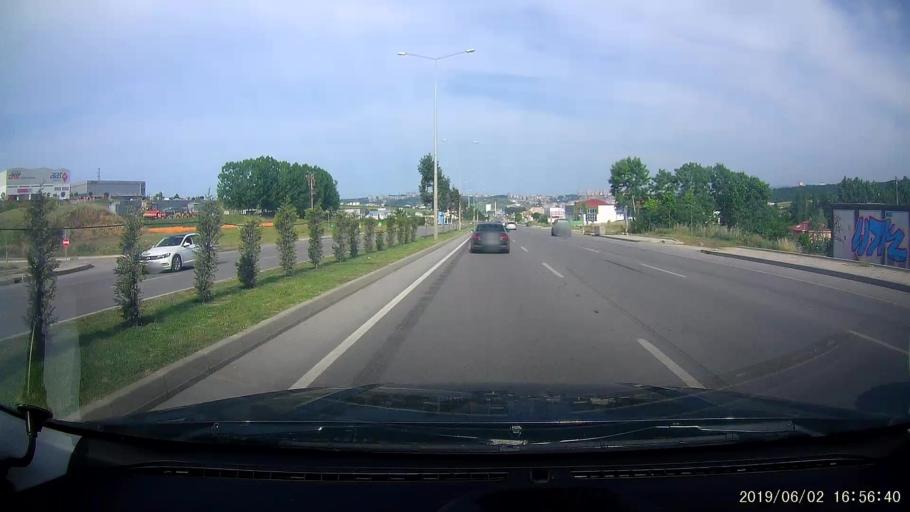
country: TR
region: Samsun
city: Samsun
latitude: 41.2921
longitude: 36.2633
